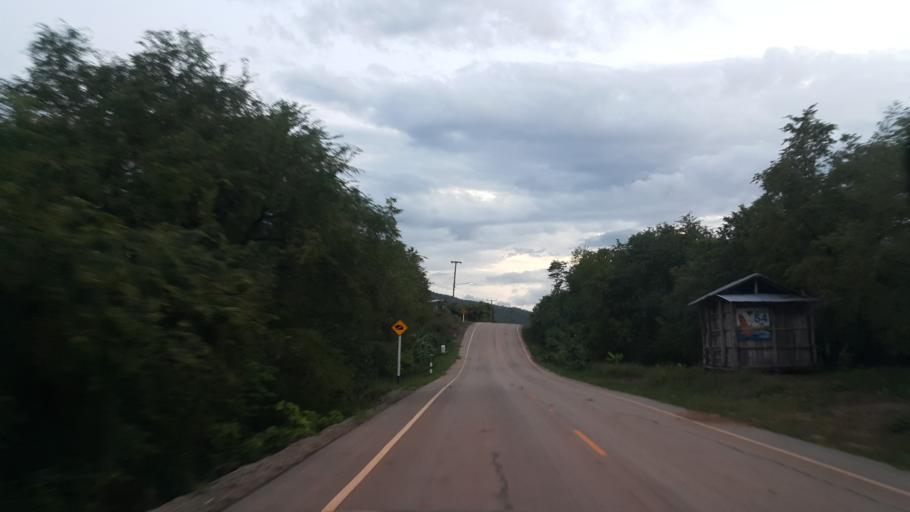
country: TH
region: Loei
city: Phu Ruea
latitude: 17.5108
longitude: 101.2331
